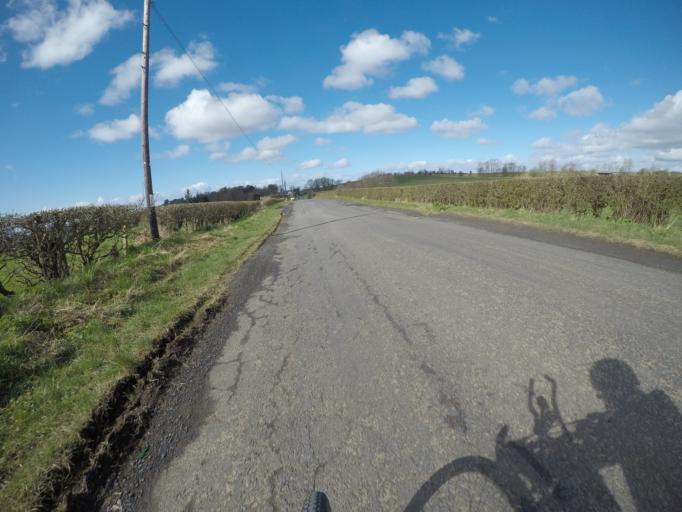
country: GB
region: Scotland
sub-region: East Ayrshire
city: Crosshouse
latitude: 55.6015
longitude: -4.5642
